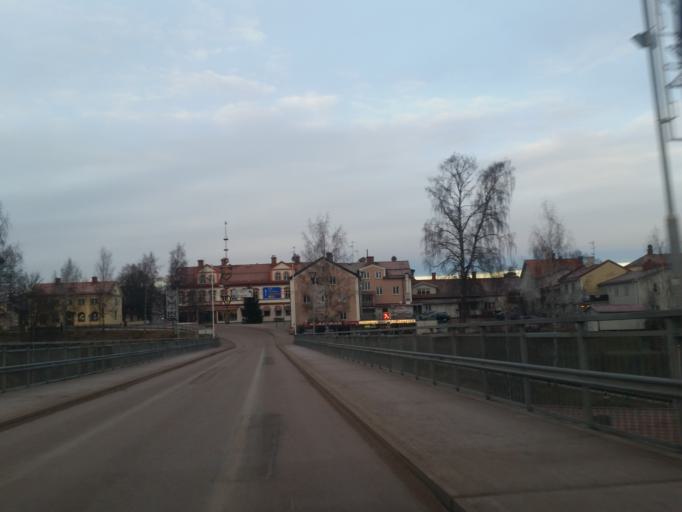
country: SE
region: Dalarna
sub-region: Leksand Municipality
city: Leksand
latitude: 60.7289
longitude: 14.9983
